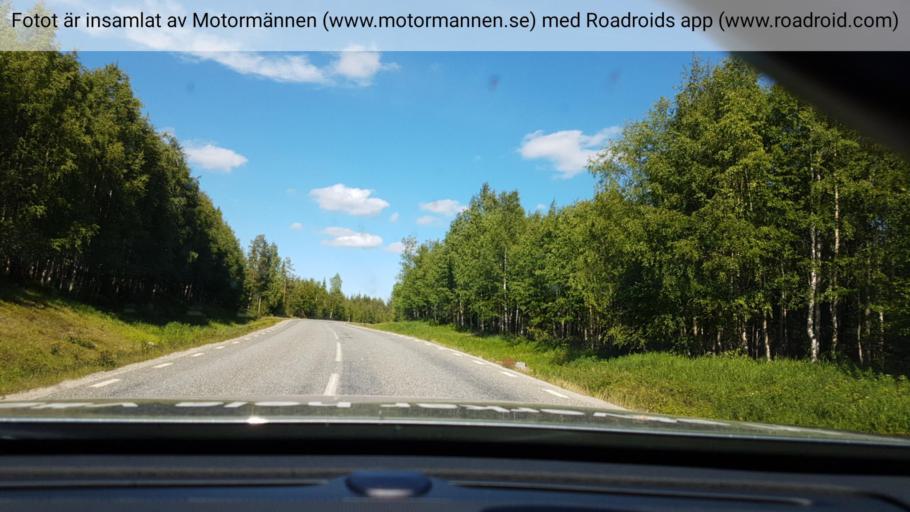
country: SE
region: Vaesterbotten
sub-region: Lycksele Kommun
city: Lycksele
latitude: 64.6213
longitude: 18.3511
